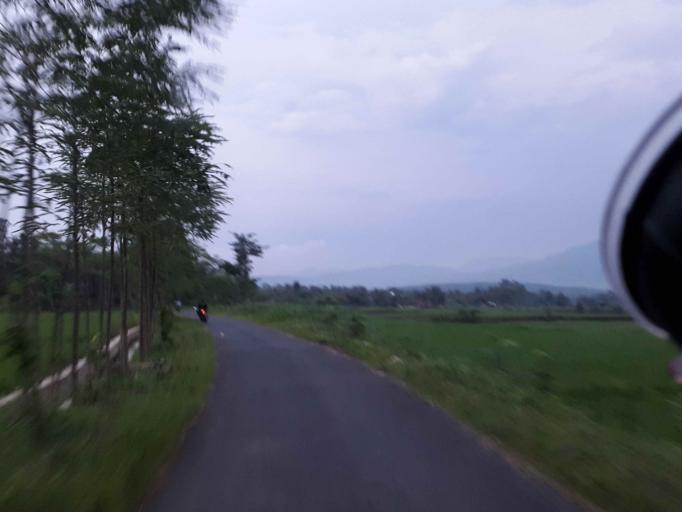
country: ID
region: Central Java
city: Randudongkal
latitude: -7.0762
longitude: 109.3371
